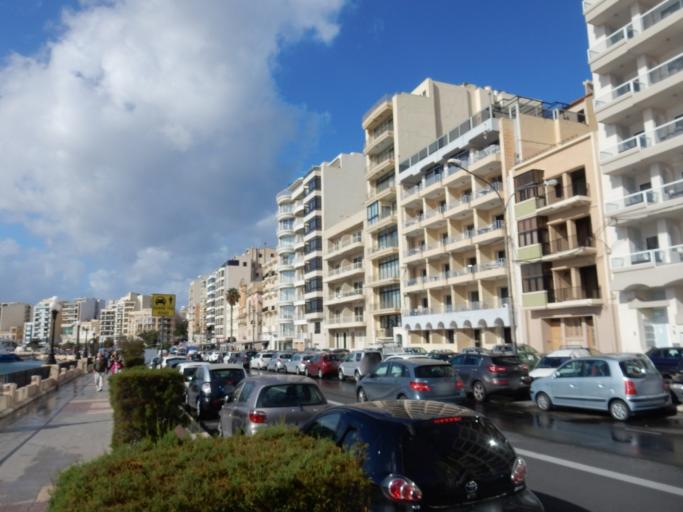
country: MT
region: Tas-Sliema
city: Sliema
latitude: 35.9073
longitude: 14.5076
